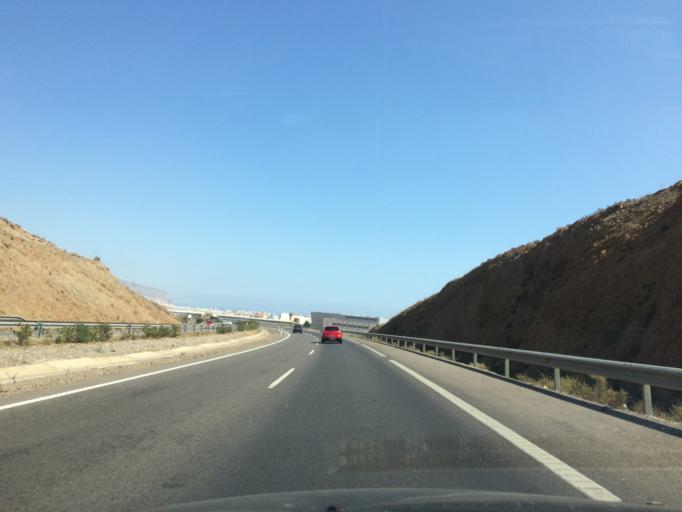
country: ES
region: Andalusia
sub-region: Provincia de Almeria
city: Vicar
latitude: 36.8109
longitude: -2.6365
